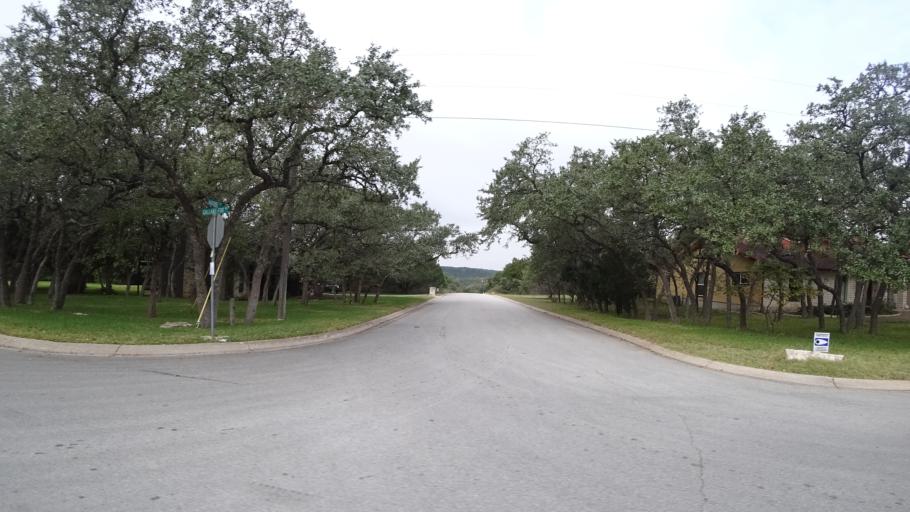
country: US
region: Texas
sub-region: Travis County
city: Shady Hollow
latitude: 30.2182
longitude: -97.8964
